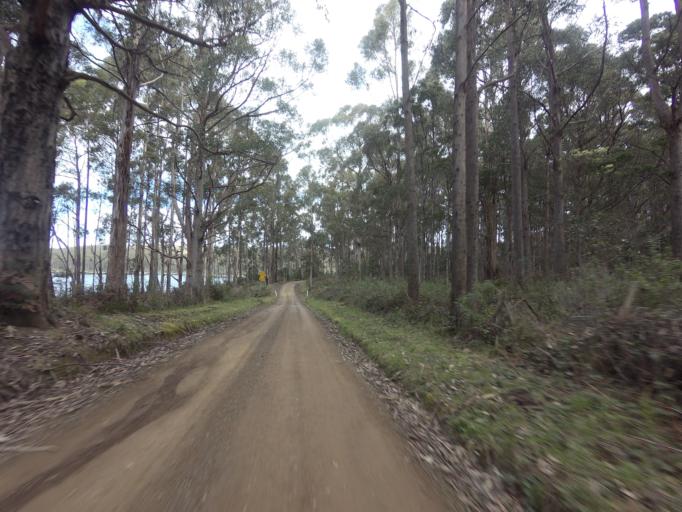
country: AU
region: Tasmania
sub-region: Huon Valley
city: Geeveston
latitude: -43.4187
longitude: 147.0143
